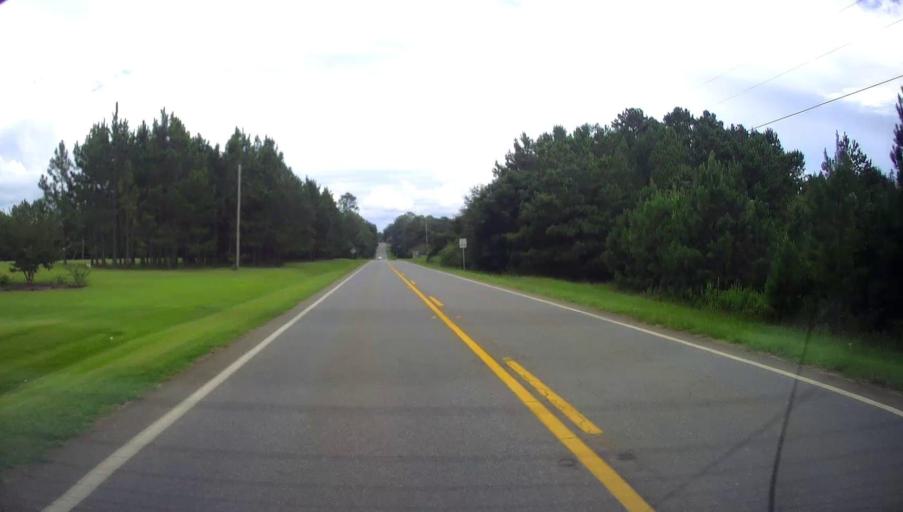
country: US
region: Georgia
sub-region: Schley County
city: Ellaville
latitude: 32.2451
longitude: -84.3212
